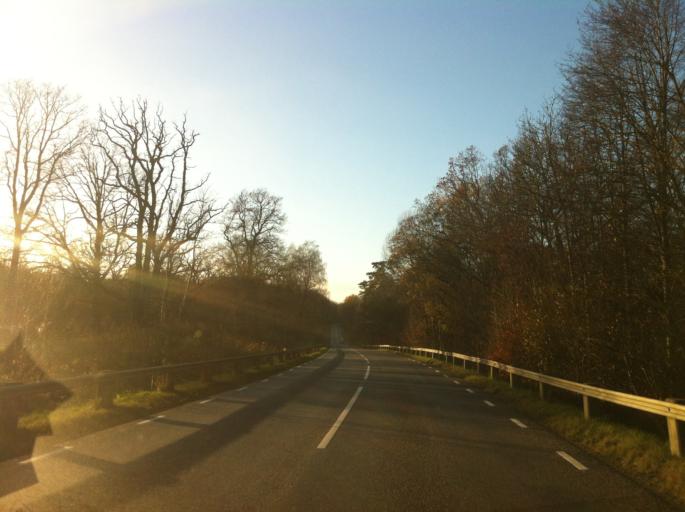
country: SE
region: Skane
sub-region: Ostra Goinge Kommun
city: Knislinge
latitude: 56.1919
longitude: 14.0872
